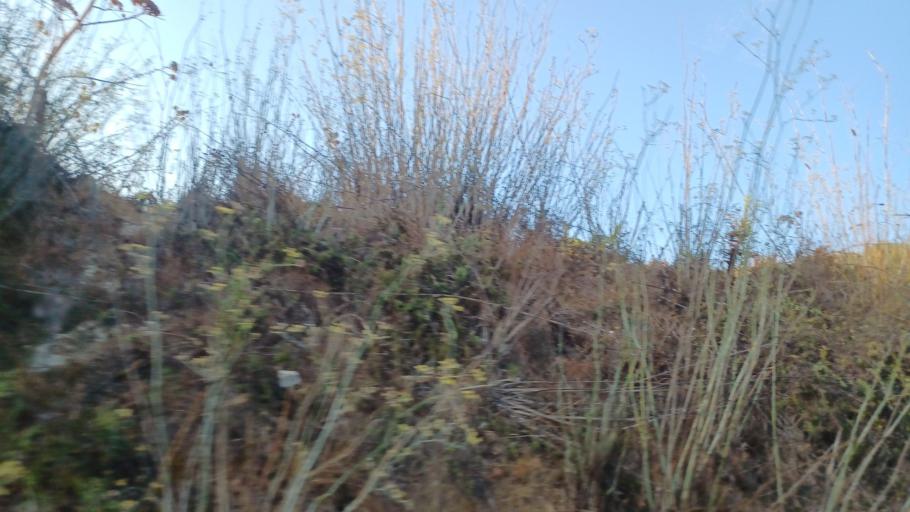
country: CY
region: Pafos
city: Mesogi
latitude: 34.8659
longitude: 32.5076
